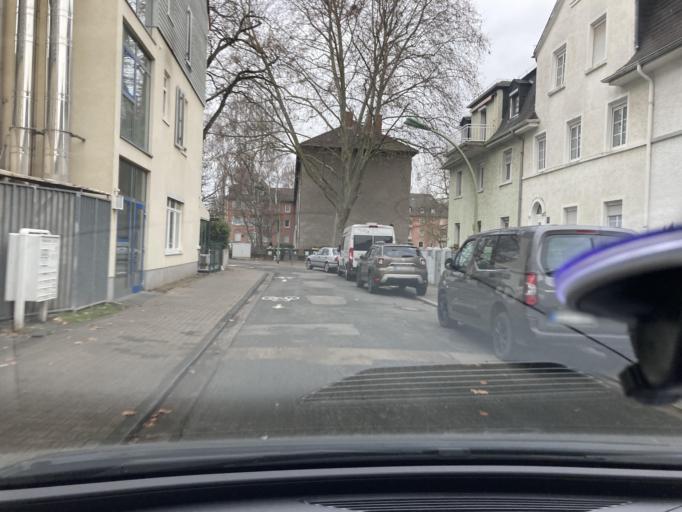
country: DE
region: Hesse
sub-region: Regierungsbezirk Darmstadt
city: Offenbach
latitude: 50.1291
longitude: 8.7320
